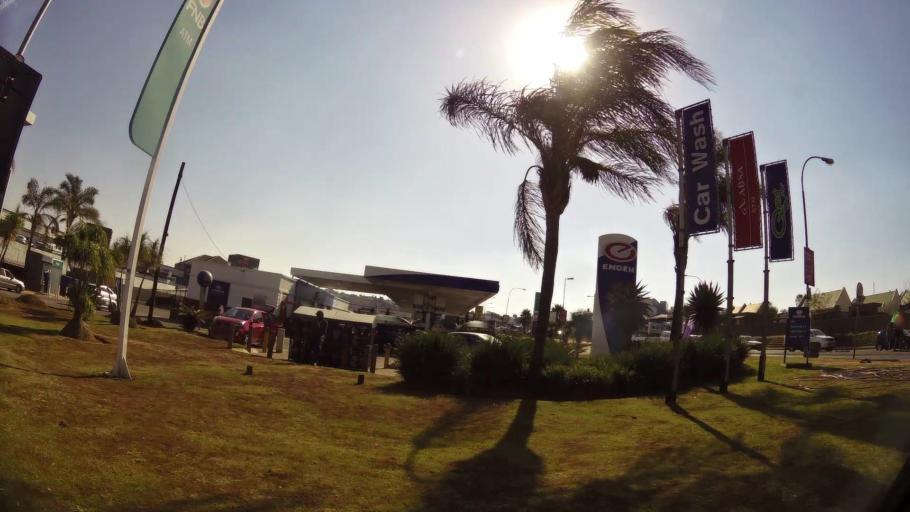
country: ZA
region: Gauteng
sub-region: City of Johannesburg Metropolitan Municipality
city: Johannesburg
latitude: -26.2663
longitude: 28.0602
